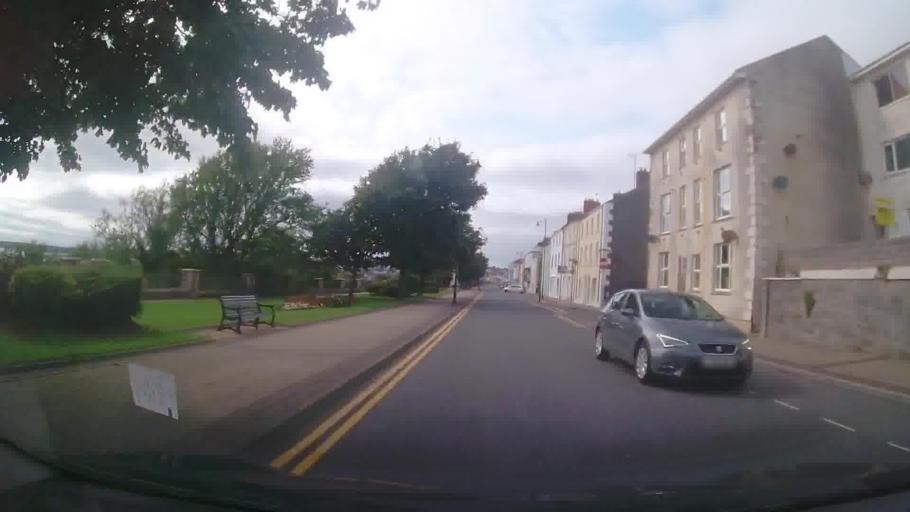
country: GB
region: Wales
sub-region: Pembrokeshire
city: Milford Haven
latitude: 51.7119
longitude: -5.0327
